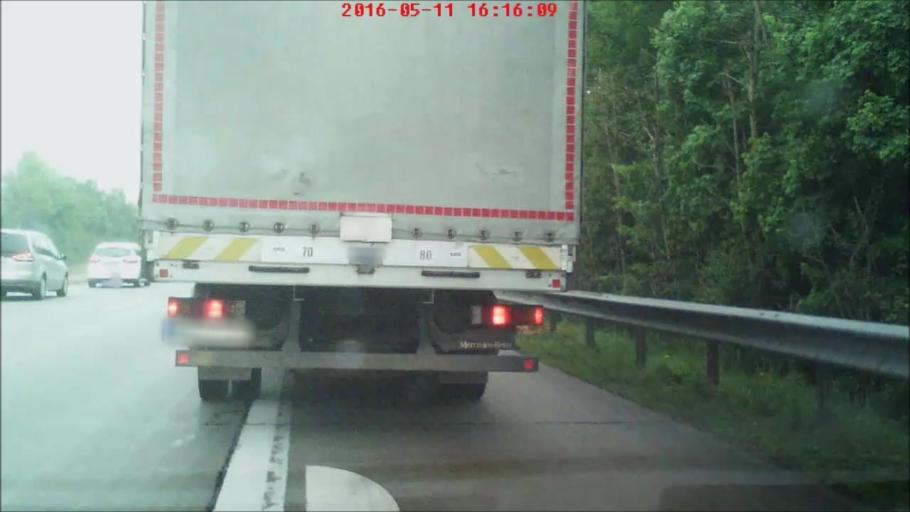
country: AT
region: Styria
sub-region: Politischer Bezirk Leibnitz
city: Gabersdorf
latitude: 46.7820
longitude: 15.5767
